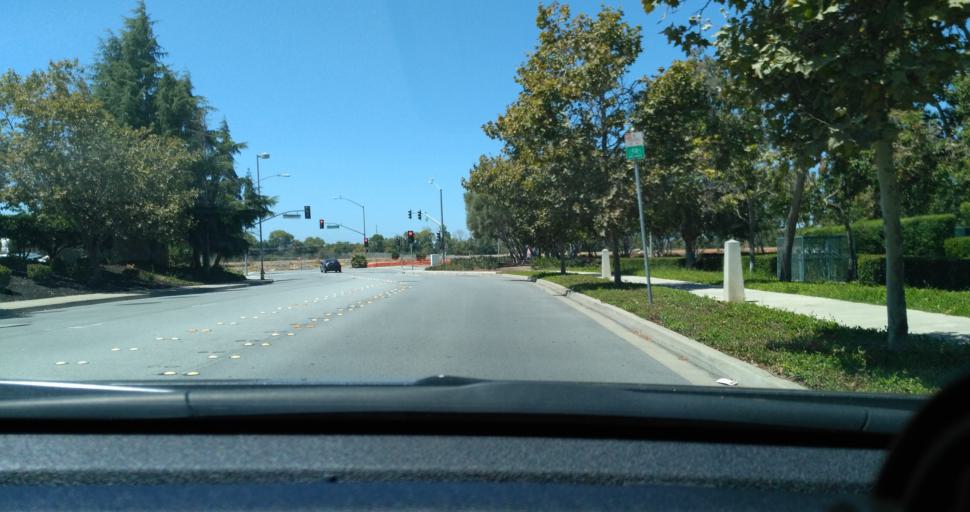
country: US
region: California
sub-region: Santa Clara County
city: Milpitas
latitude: 37.4327
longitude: -121.9208
